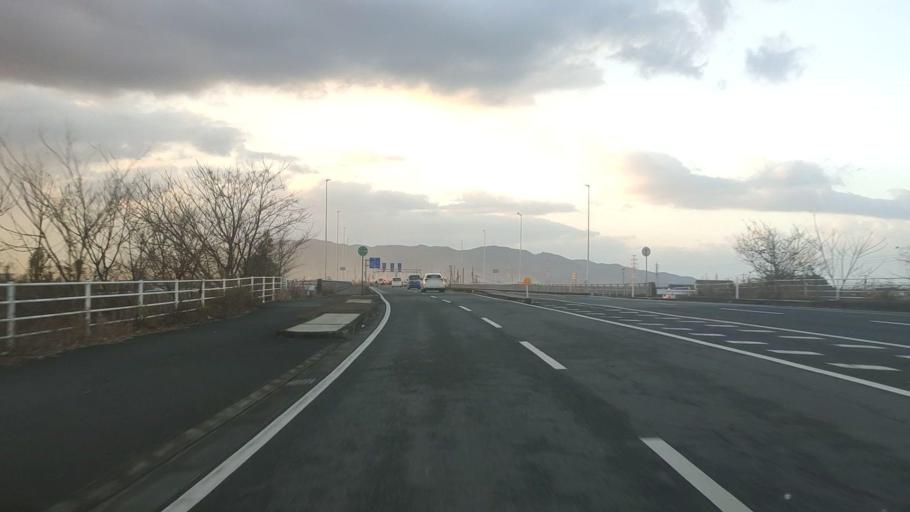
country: JP
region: Kumamoto
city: Kumamoto
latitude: 32.7414
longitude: 130.7047
